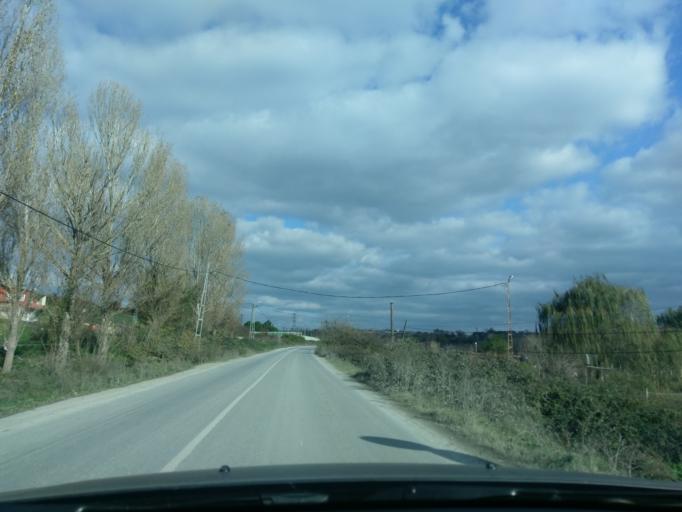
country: TR
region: Istanbul
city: Durusu
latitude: 41.2959
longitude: 28.6685
